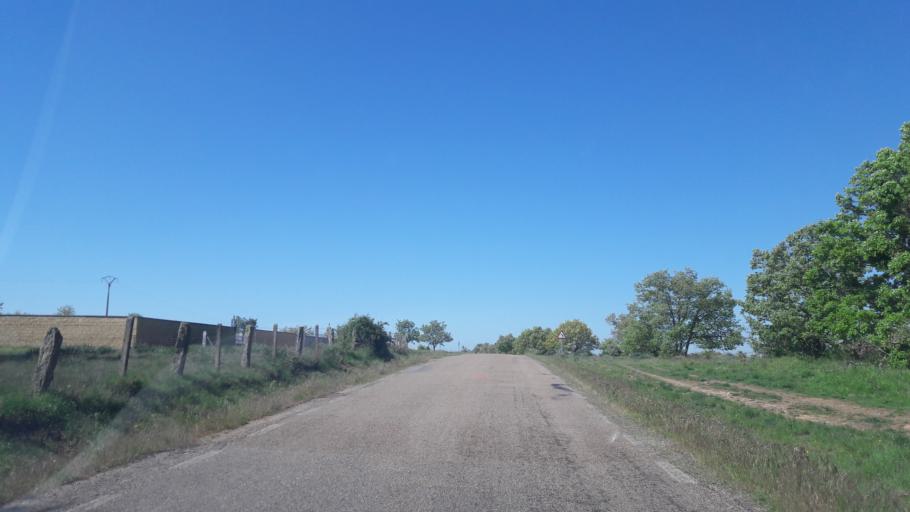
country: ES
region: Castille and Leon
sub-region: Provincia de Salamanca
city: Banobarez
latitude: 40.8565
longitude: -6.6041
